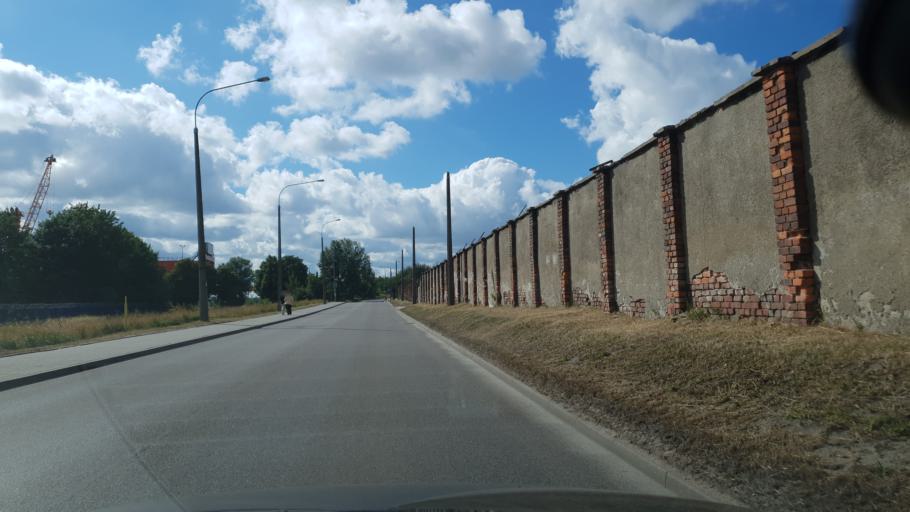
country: PL
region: Pomeranian Voivodeship
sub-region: Gdynia
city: Gdynia
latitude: 54.5452
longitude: 18.5237
